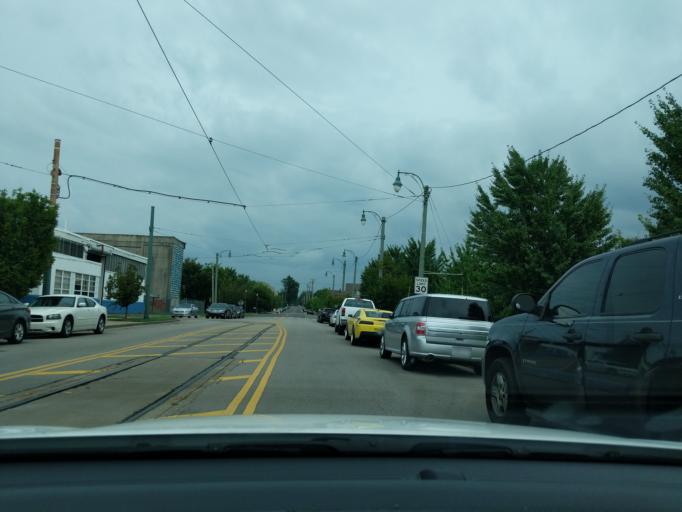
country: US
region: Tennessee
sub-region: Shelby County
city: Memphis
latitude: 35.1592
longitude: -90.0472
